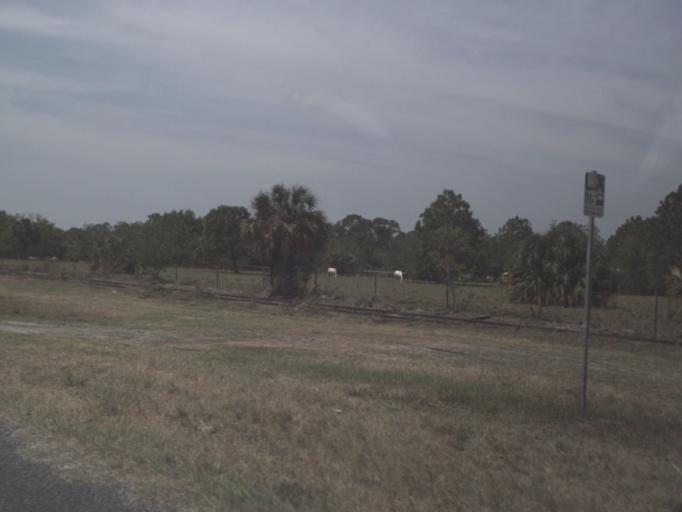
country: US
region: Florida
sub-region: Lake County
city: Umatilla
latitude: 28.9016
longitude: -81.6857
